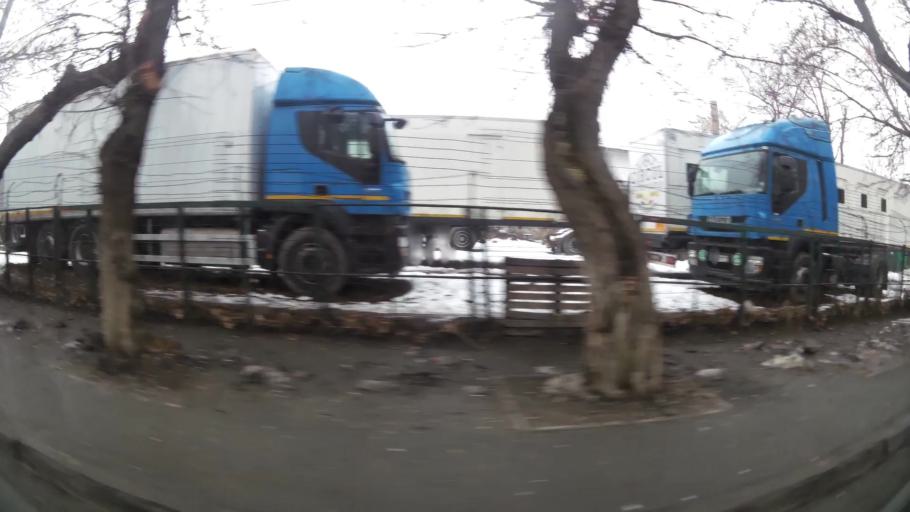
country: RO
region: Ilfov
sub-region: Comuna Chiajna
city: Rosu
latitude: 44.4692
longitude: 26.0265
